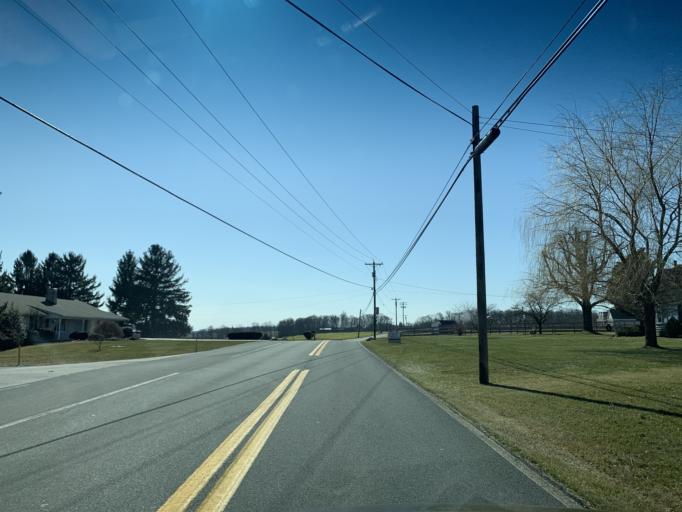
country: US
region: Maryland
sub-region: Carroll County
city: Hampstead
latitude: 39.5853
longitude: -76.8662
